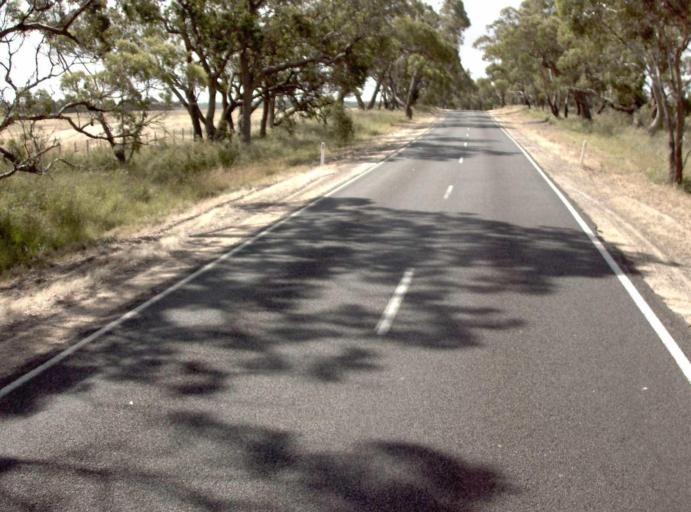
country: AU
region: Victoria
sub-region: Wellington
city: Sale
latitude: -38.2853
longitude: 147.1544
